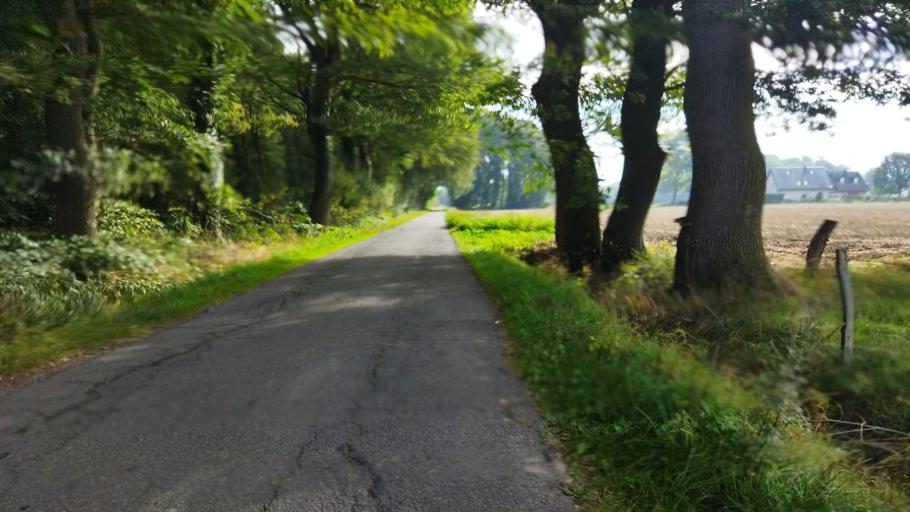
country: DE
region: Lower Saxony
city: Bad Rothenfelde
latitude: 52.0793
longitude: 8.1563
